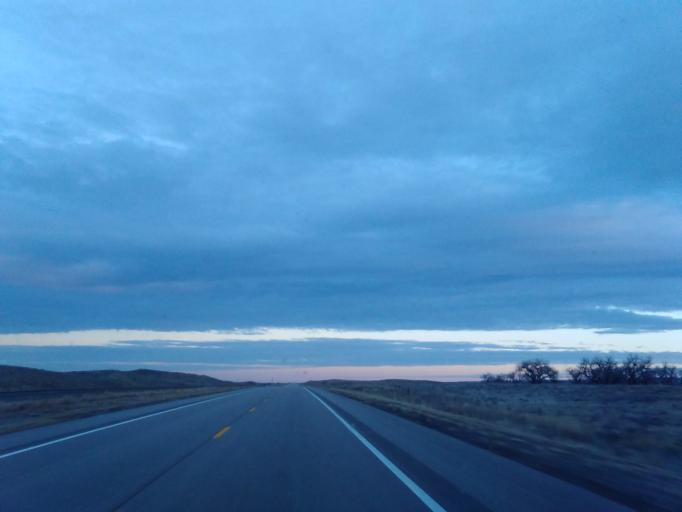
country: US
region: Nebraska
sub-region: Garden County
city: Oshkosh
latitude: 41.3786
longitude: -102.2652
